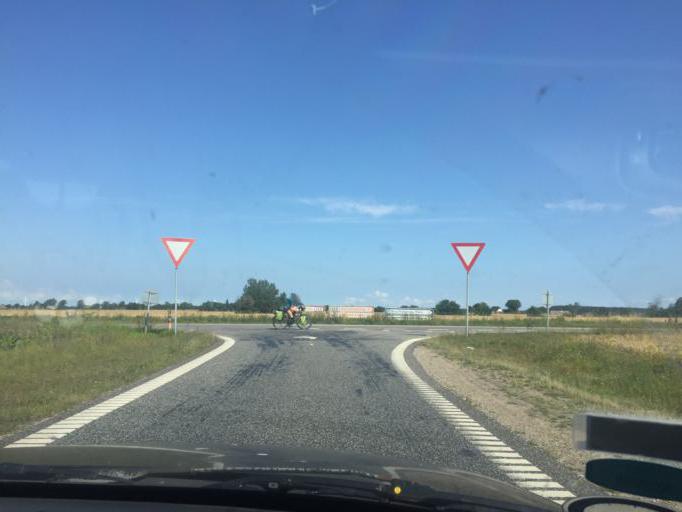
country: DK
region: Zealand
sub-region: Guldborgsund Kommune
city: Sakskobing
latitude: 54.7894
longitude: 11.5680
